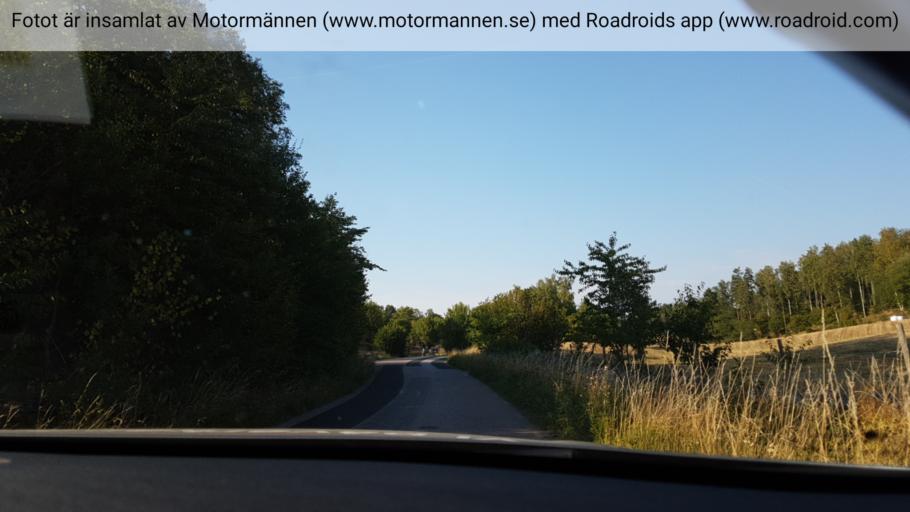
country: SE
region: Vaestra Goetaland
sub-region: Skovde Kommun
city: Skoevde
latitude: 58.4620
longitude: 13.7394
